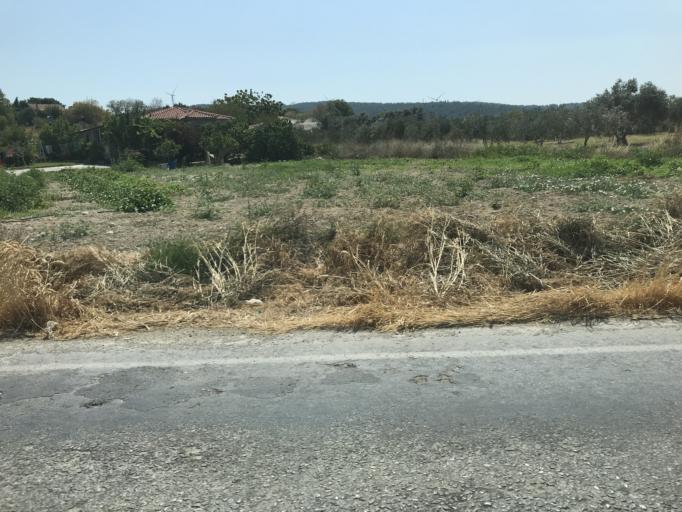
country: TR
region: Izmir
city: Urla
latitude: 38.3077
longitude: 26.7547
